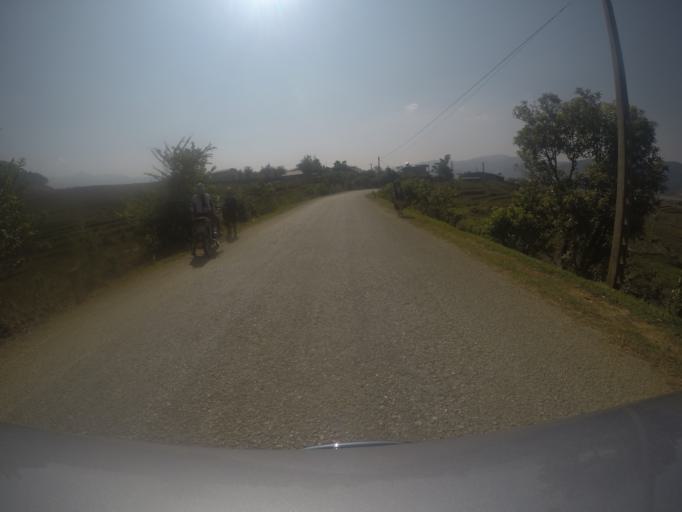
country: VN
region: Lai Chau
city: Than Uyen
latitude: 22.0226
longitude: 103.9335
